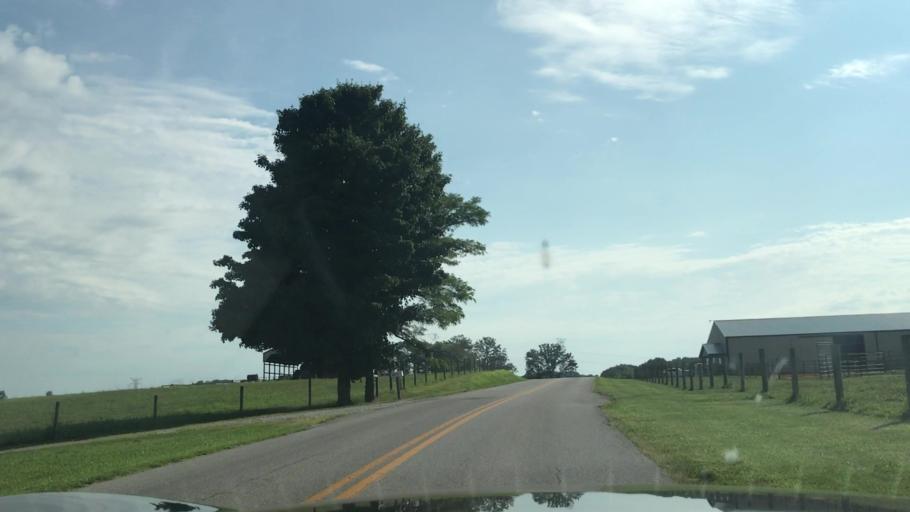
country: US
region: Kentucky
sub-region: Hart County
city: Munfordville
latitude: 37.2270
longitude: -85.7180
